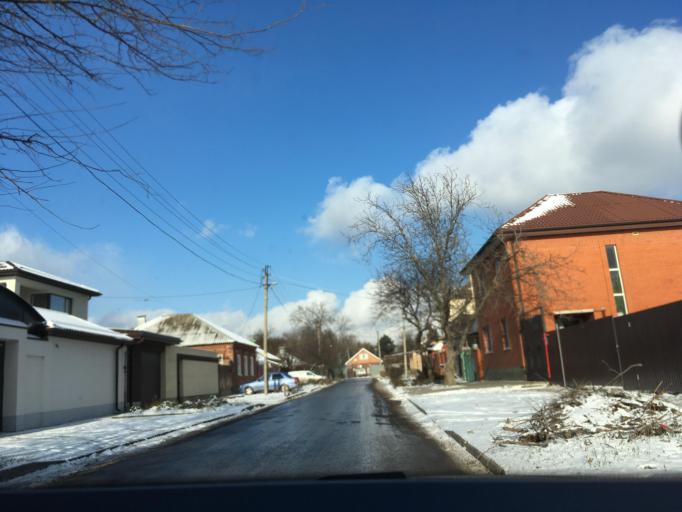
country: RU
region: Rostov
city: Rostov-na-Donu
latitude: 47.2349
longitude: 39.6295
